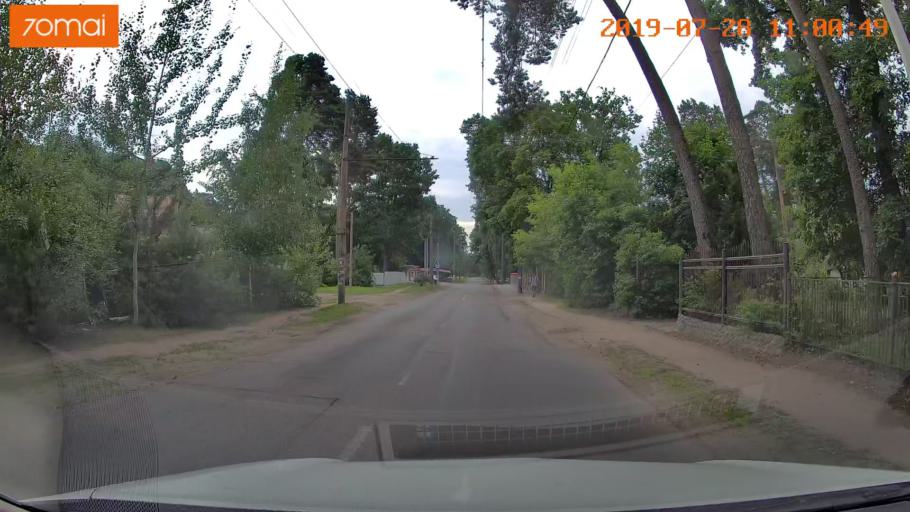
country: RU
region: Kaliningrad
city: Vzmorye
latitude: 54.7251
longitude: 20.3640
